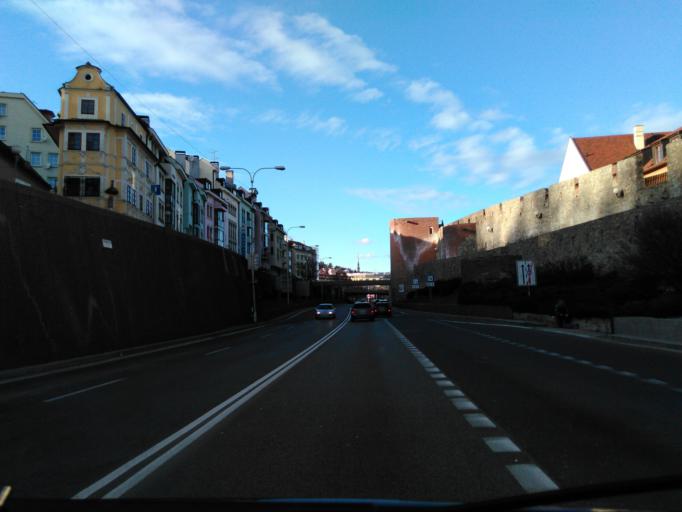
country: SK
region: Bratislavsky
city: Bratislava
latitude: 48.1420
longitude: 17.1044
